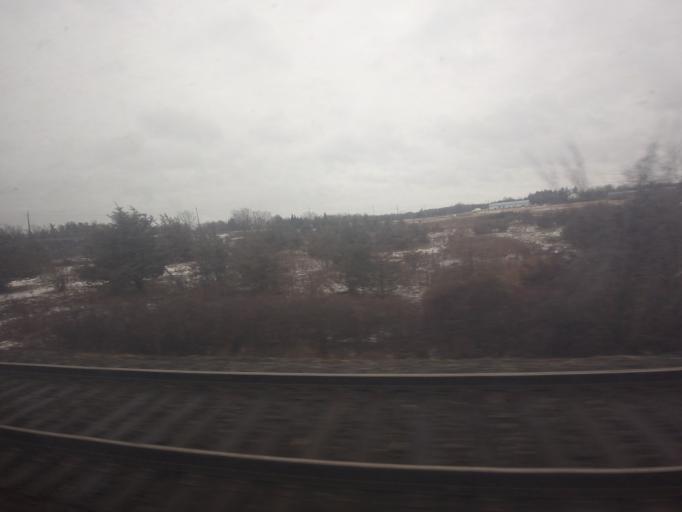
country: CA
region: Ontario
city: Kingston
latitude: 44.2304
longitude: -76.6730
